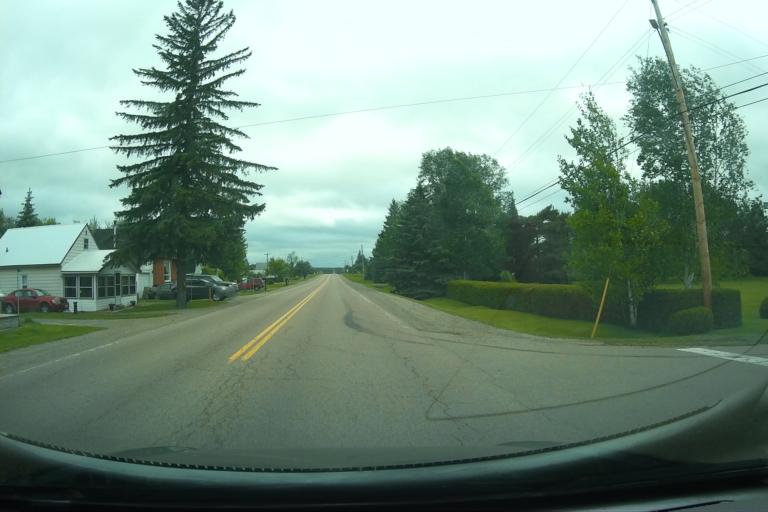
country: CA
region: Ontario
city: Pembroke
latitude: 45.5313
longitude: -77.0998
